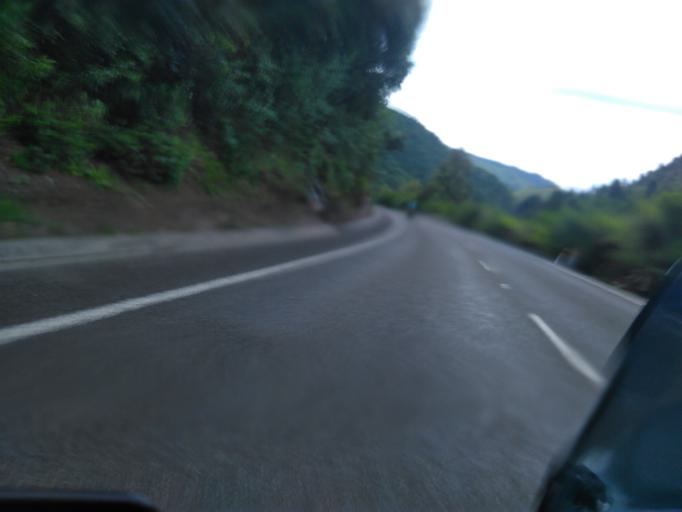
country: NZ
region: Bay of Plenty
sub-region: Opotiki District
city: Opotiki
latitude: -38.2462
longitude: 177.3040
